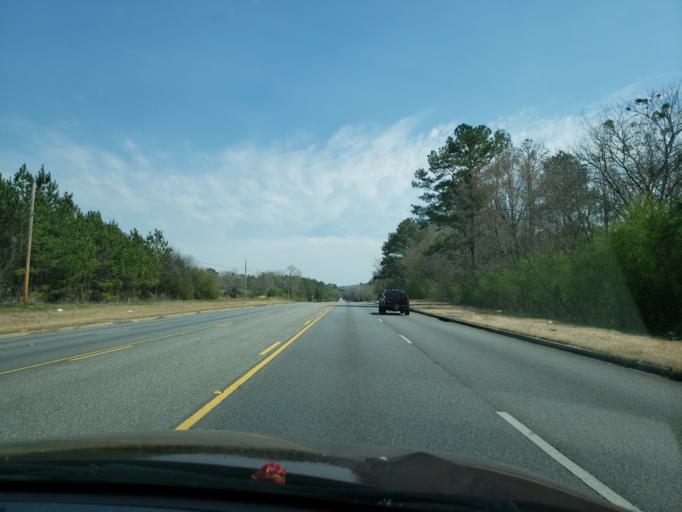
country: US
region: Alabama
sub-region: Elmore County
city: Wetumpka
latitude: 32.5341
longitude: -86.2463
